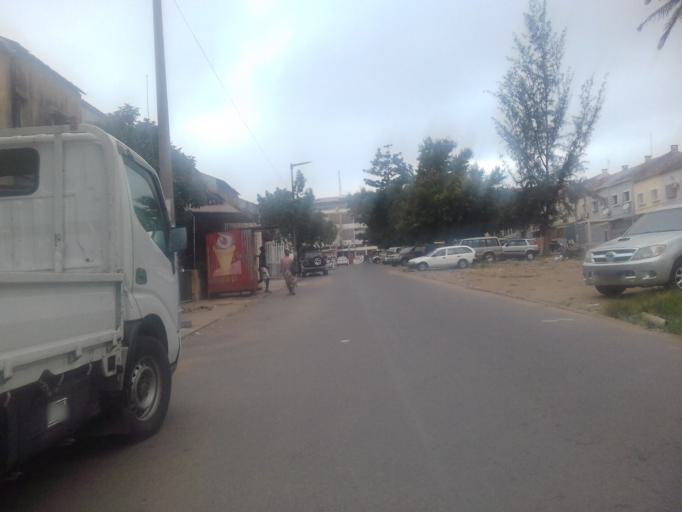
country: MZ
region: Maputo City
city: Maputo
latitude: -25.9538
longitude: 32.5832
